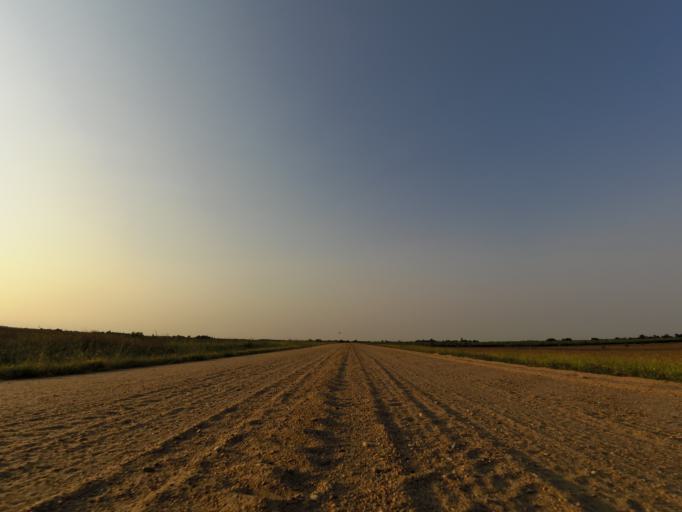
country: US
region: Kansas
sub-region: Reno County
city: South Hutchinson
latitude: 37.9709
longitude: -97.9957
